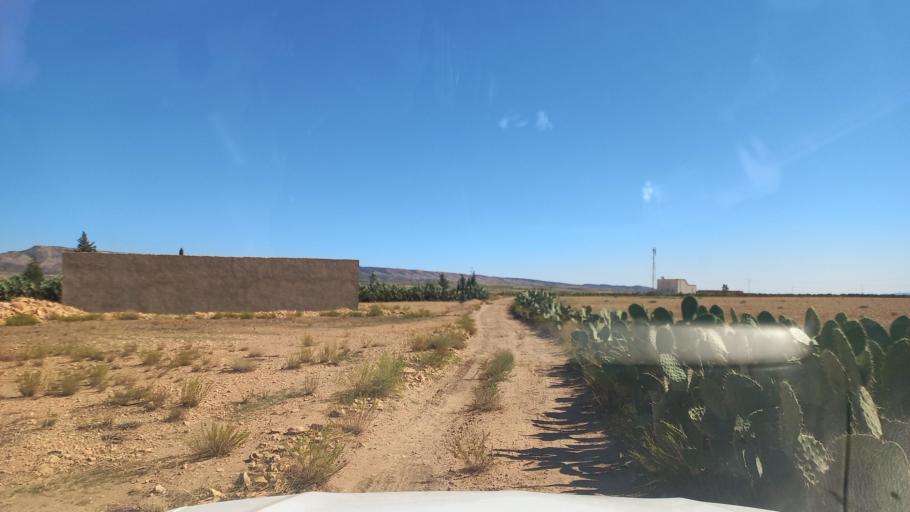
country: TN
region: Al Qasrayn
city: Sbiba
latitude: 35.3842
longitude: 9.0939
